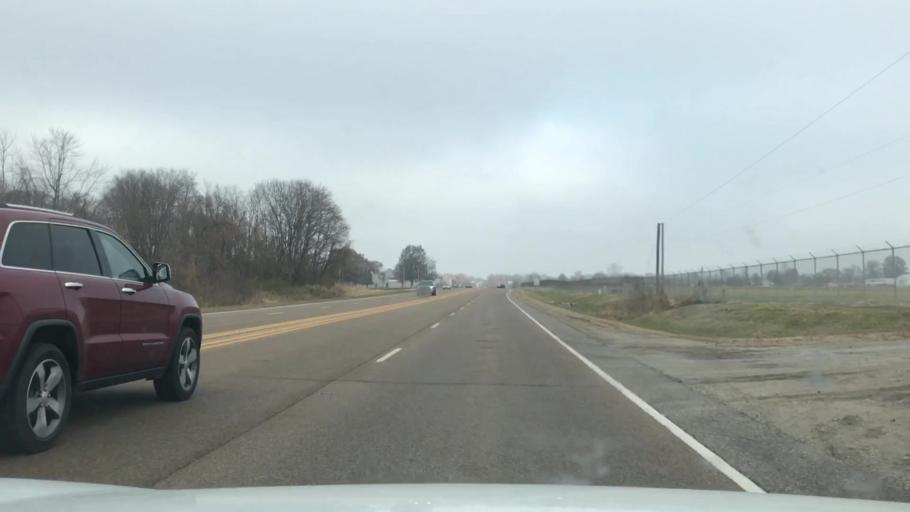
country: US
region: Illinois
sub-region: Madison County
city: Bethalto
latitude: 38.8942
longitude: -90.0592
